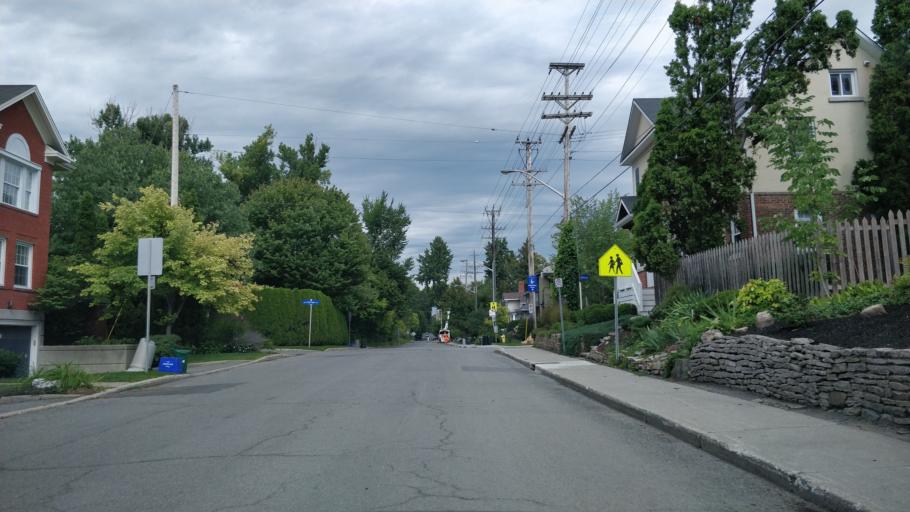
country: CA
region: Ontario
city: Ottawa
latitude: 45.4441
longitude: -75.6774
